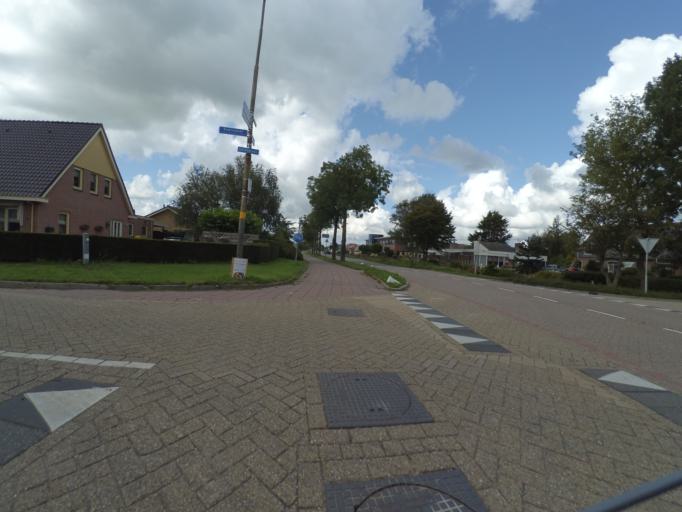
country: NL
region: North Holland
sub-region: Gemeente Schagen
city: Harenkarspel
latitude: 52.7272
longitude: 4.8283
